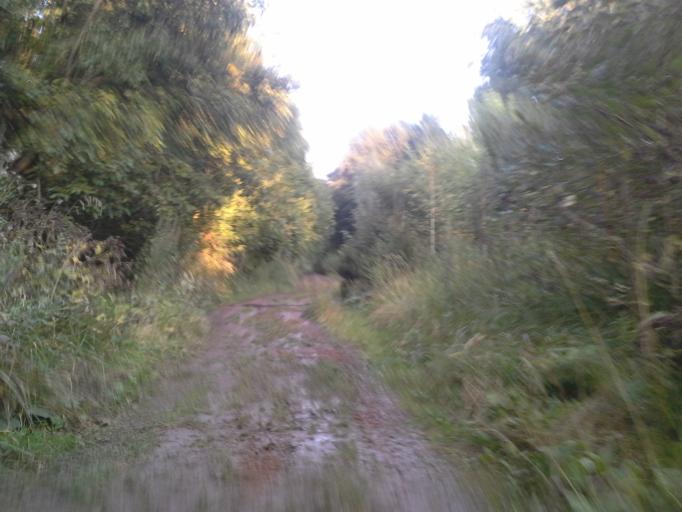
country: RU
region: Moskovskaya
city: Vatutinki
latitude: 55.5135
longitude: 37.3828
